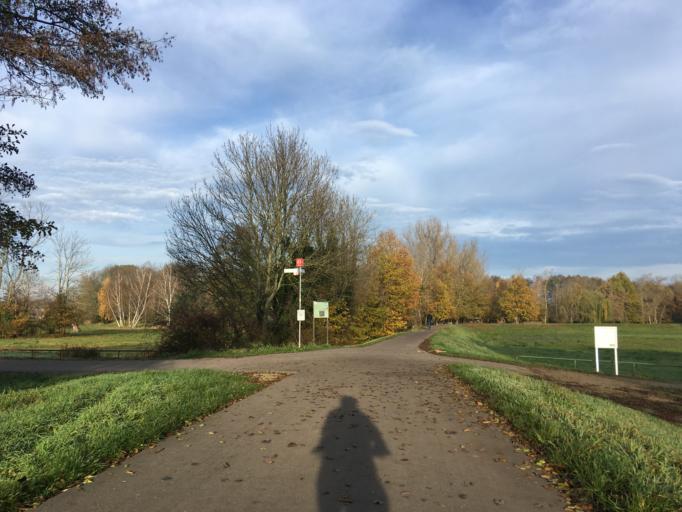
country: DE
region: Brandenburg
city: Luebben
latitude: 51.9337
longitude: 13.8999
